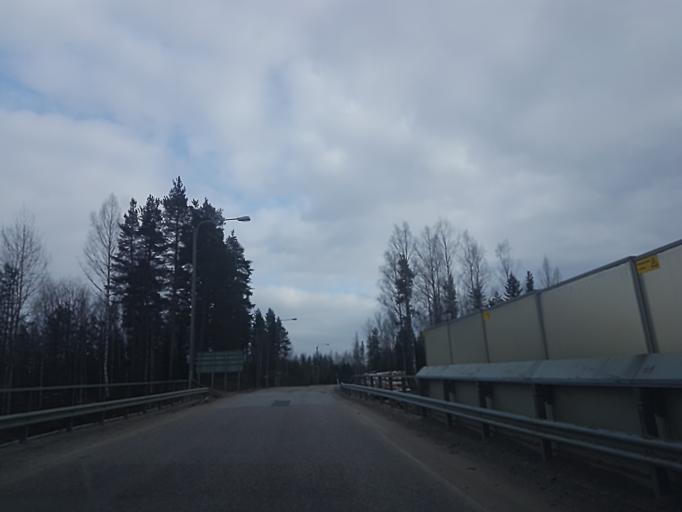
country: FI
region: South Karelia
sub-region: Imatra
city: Parikkala
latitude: 61.5293
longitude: 29.5184
